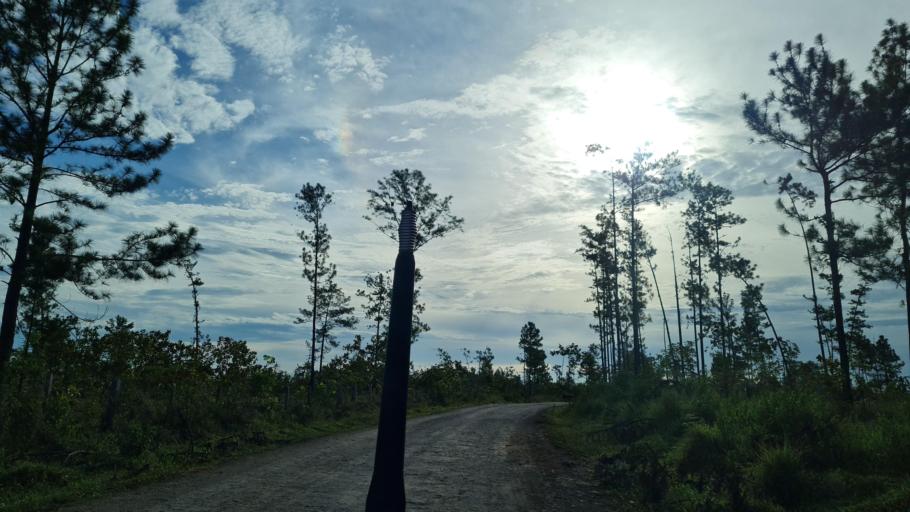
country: NI
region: Atlantico Sur
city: La Cruz de Rio Grande
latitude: 13.5558
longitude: -84.2919
